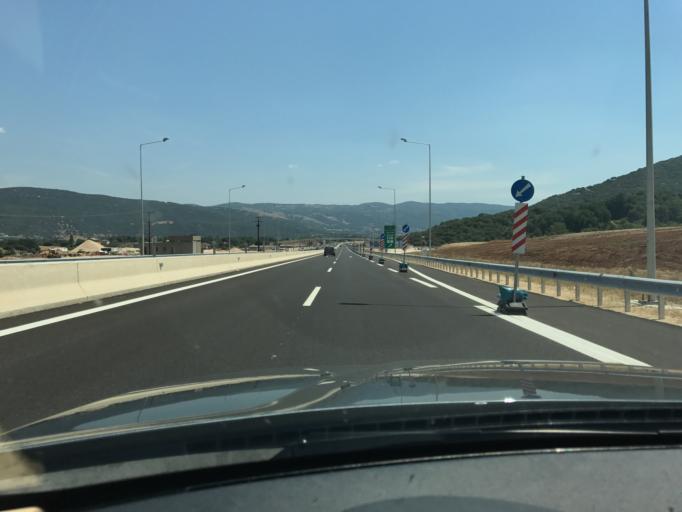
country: GR
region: Epirus
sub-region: Nomos Ioanninon
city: Agia Kyriaki
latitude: 39.5466
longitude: 20.8477
